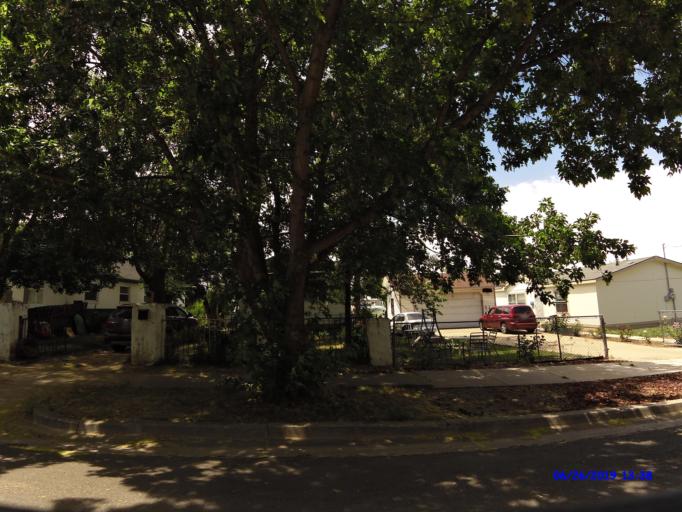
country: US
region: Utah
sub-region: Weber County
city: South Ogden
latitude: 41.2053
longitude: -111.9639
